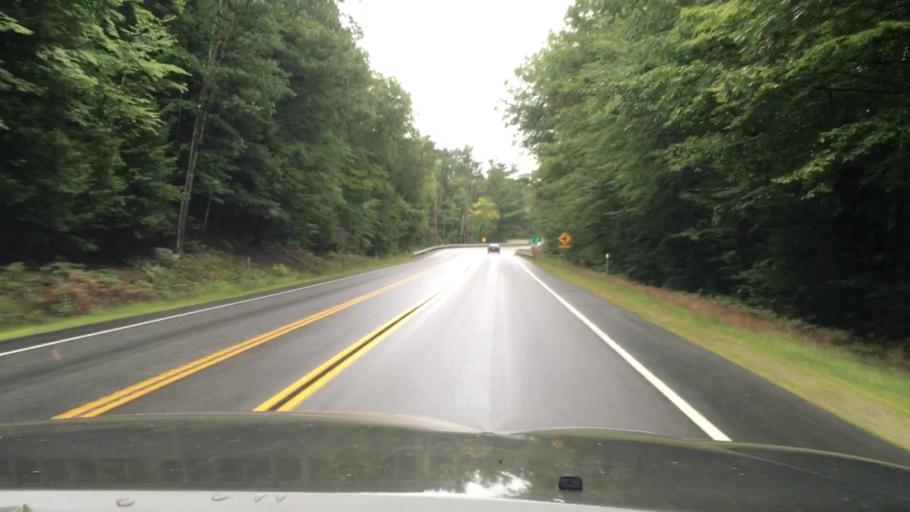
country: US
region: New Hampshire
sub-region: Hillsborough County
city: Antrim
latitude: 43.0777
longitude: -71.9798
